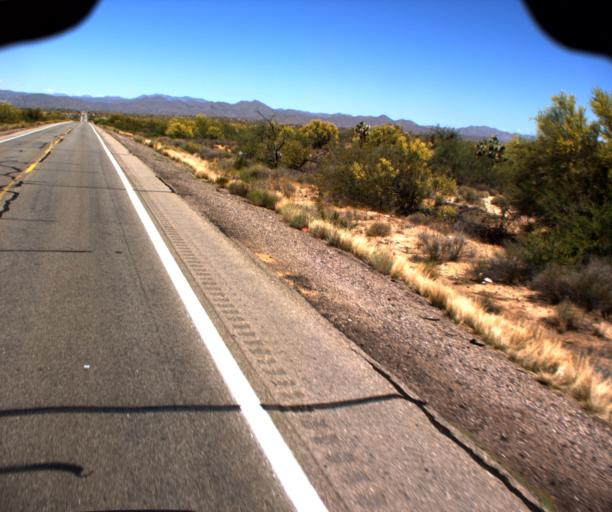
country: US
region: Arizona
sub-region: Yavapai County
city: Bagdad
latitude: 34.3199
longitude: -113.1343
